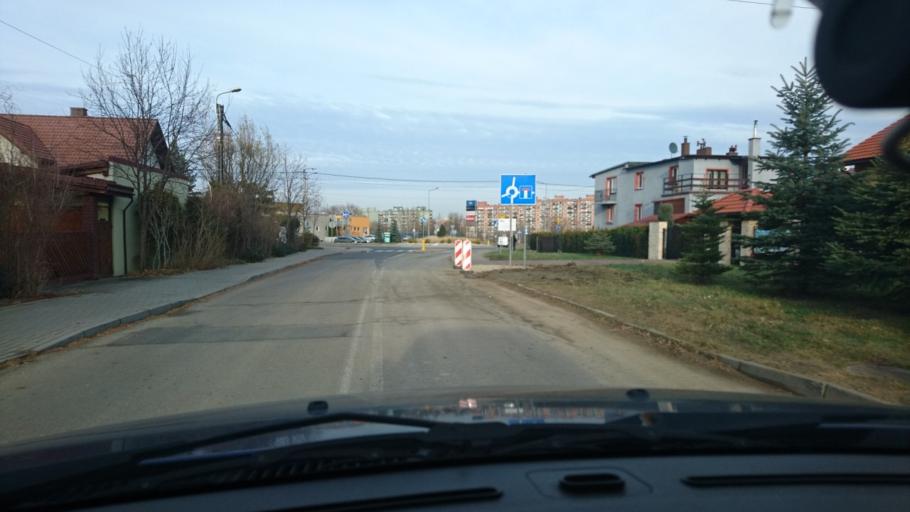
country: PL
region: Silesian Voivodeship
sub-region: Bielsko-Biala
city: Bielsko-Biala
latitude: 49.7998
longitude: 19.0291
